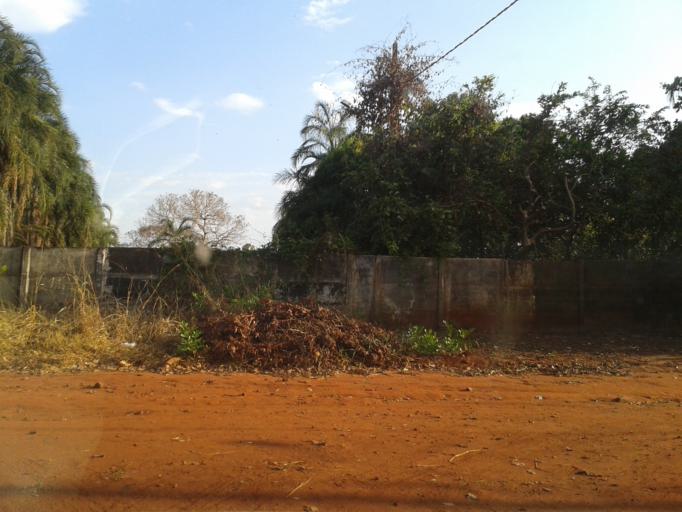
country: BR
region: Minas Gerais
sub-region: Ituiutaba
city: Ituiutaba
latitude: -18.9992
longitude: -49.4365
